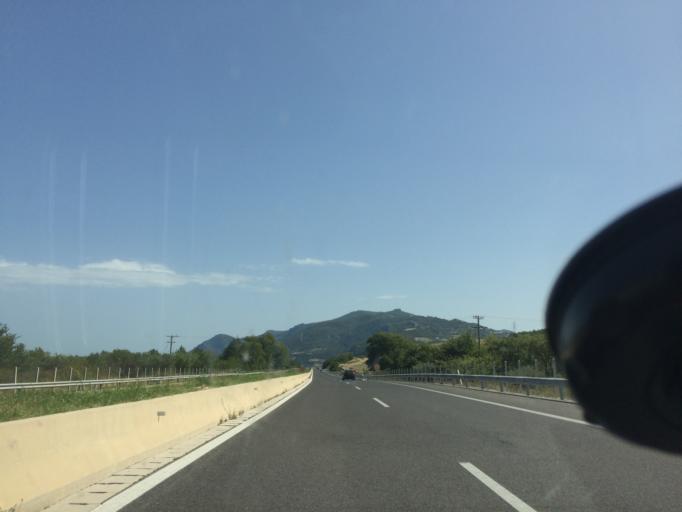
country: GR
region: Central Greece
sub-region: Nomos Fthiotidos
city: Kainouryion
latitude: 38.7896
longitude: 22.6869
